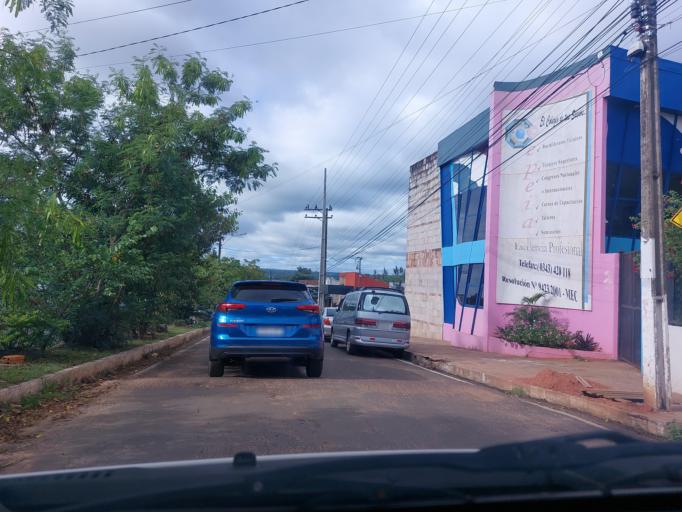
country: PY
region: San Pedro
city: Guayaybi
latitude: -24.6654
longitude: -56.4384
